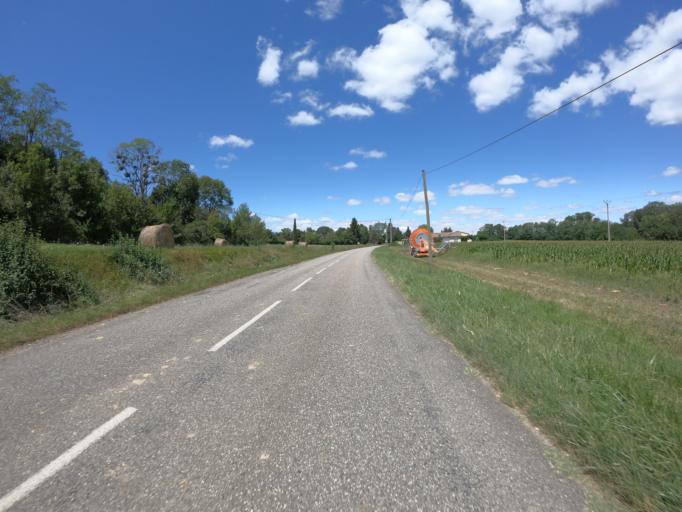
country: FR
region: Midi-Pyrenees
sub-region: Departement de l'Ariege
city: Verniolle
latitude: 43.0640
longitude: 1.7387
